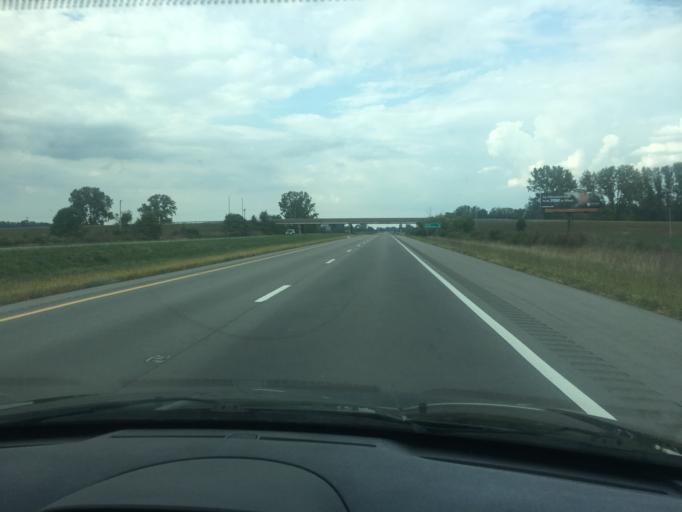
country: US
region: Ohio
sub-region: Clark County
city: Northridge
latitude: 40.0038
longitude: -83.8100
